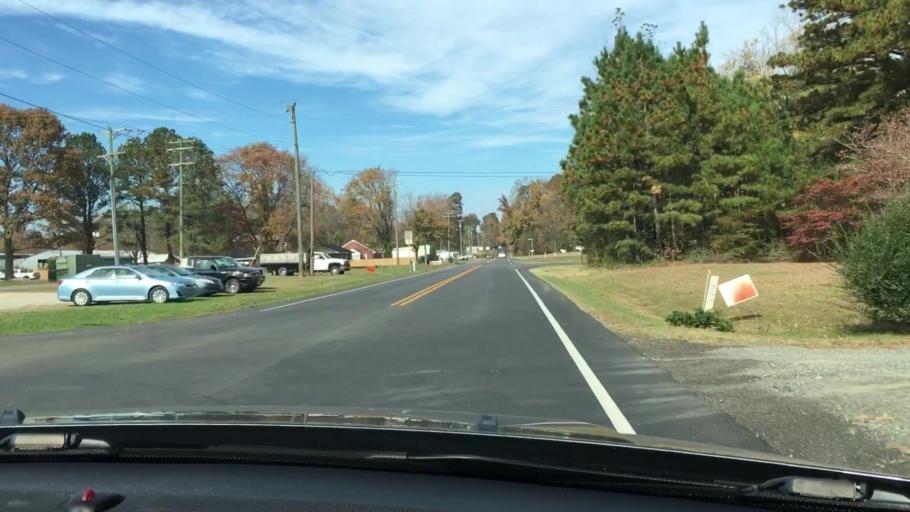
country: US
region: Virginia
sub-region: King William County
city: West Point
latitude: 37.4537
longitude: -76.8406
